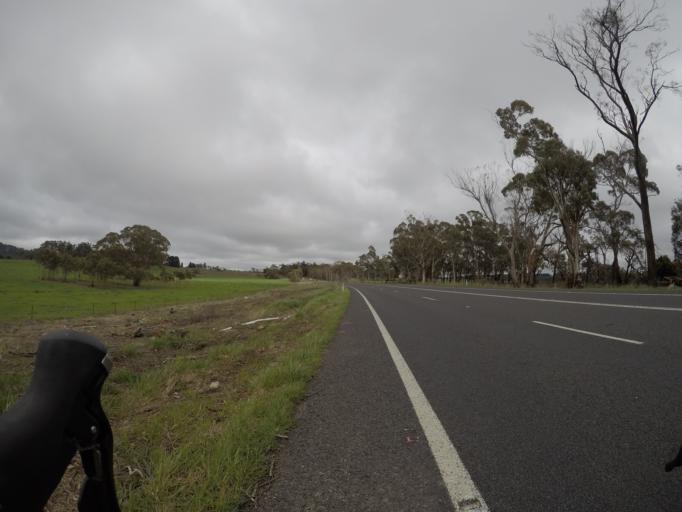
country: AU
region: New South Wales
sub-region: Lithgow
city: Portland
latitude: -33.4458
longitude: 149.9952
